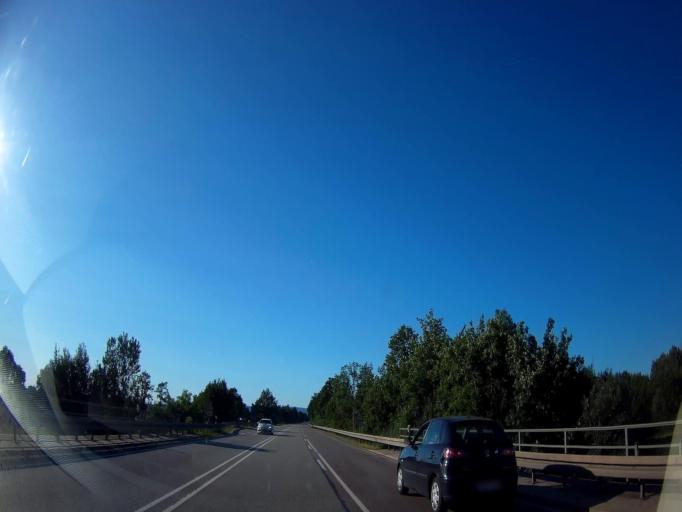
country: DE
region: Bavaria
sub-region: Lower Bavaria
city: Parkstetten
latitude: 48.8853
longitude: 12.6191
